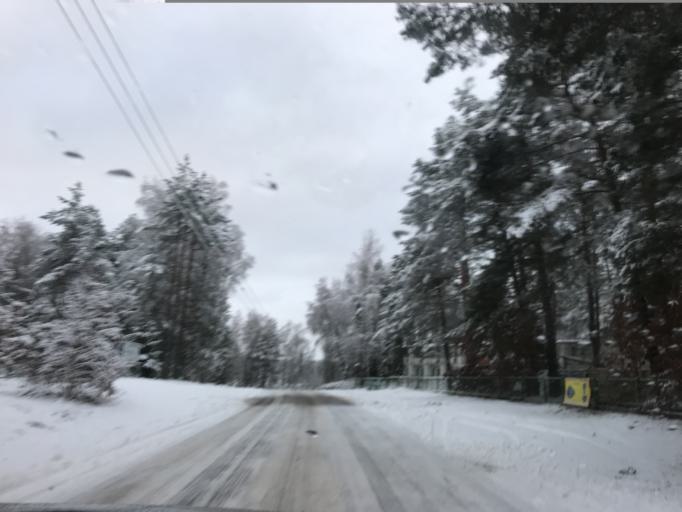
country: PL
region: Pomeranian Voivodeship
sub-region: Powiat bytowski
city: Czarna Dabrowka
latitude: 54.2808
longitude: 17.5936
